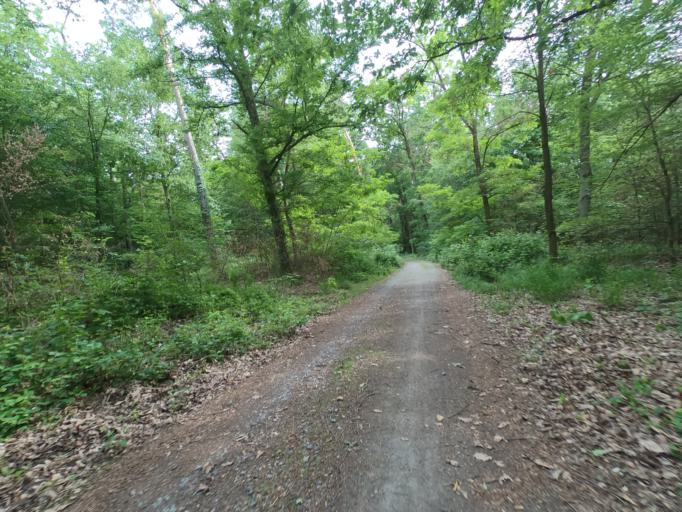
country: DE
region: Hesse
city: Niederrad
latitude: 50.0395
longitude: 8.6422
